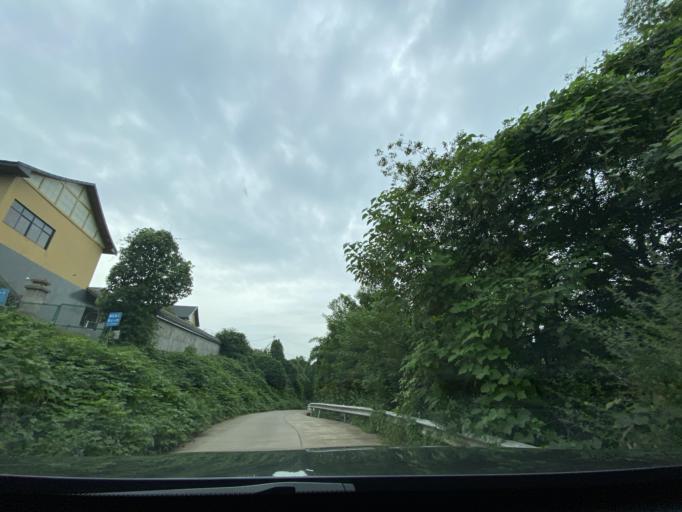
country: CN
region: Sichuan
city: Jiancheng
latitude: 30.3866
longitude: 104.4928
